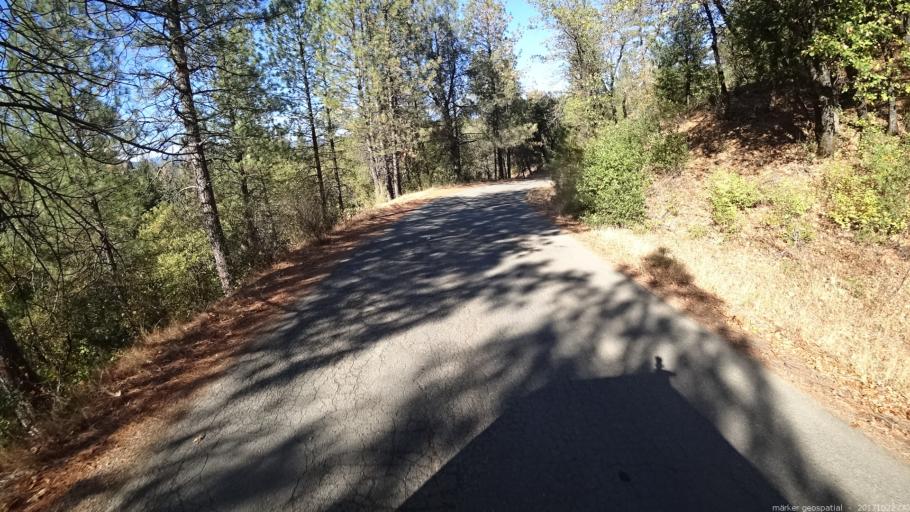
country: US
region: California
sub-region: Shasta County
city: Shasta Lake
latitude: 40.8755
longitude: -122.3647
